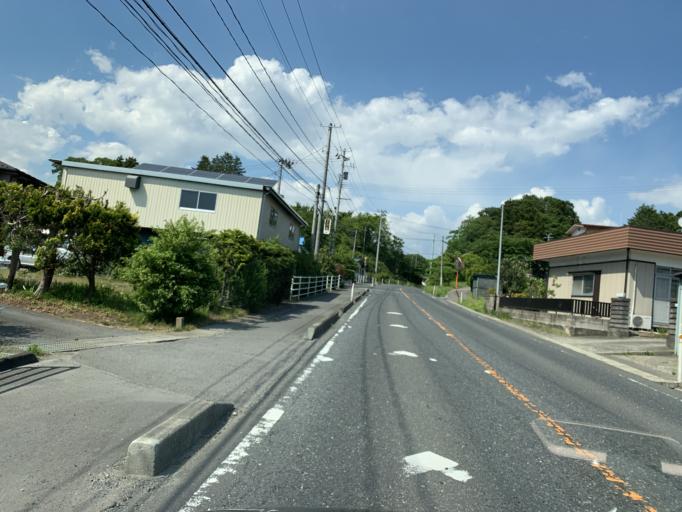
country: JP
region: Miyagi
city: Wakuya
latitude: 38.4899
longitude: 141.1083
